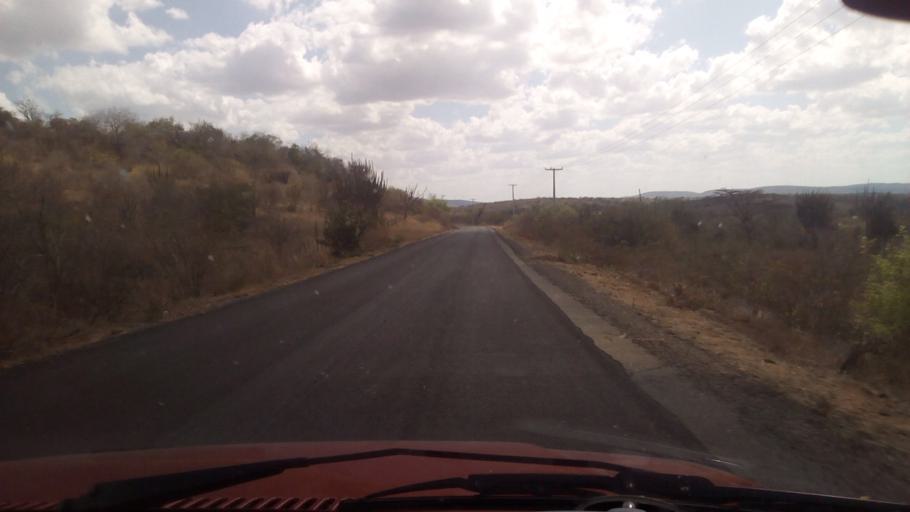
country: BR
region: Paraiba
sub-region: Cacimba De Dentro
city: Cacimba de Dentro
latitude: -6.6828
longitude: -35.7435
